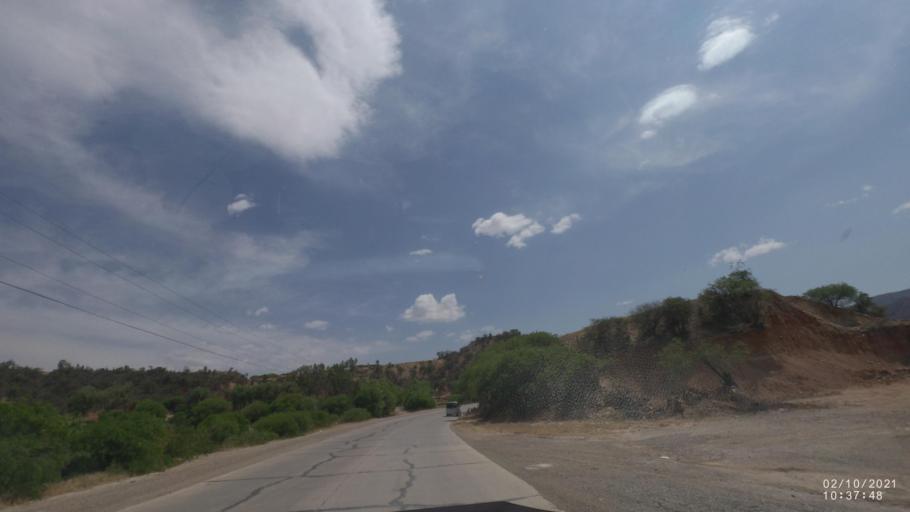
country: BO
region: Cochabamba
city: Capinota
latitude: -17.6393
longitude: -66.2661
